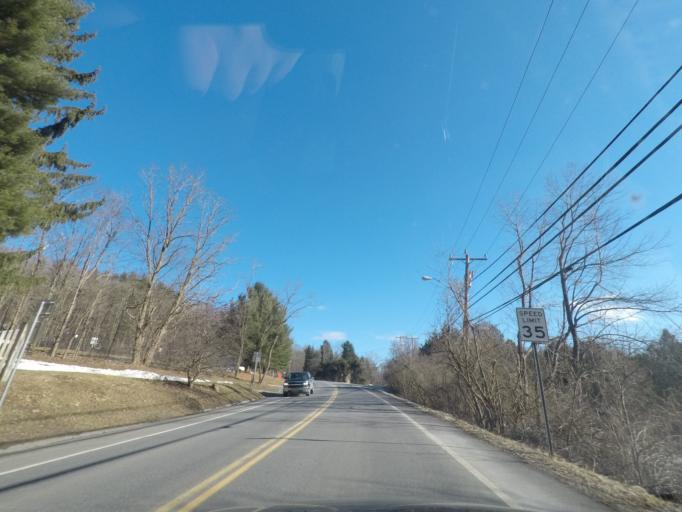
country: US
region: New York
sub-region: Columbia County
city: Chatham
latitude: 42.3216
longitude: -73.5433
